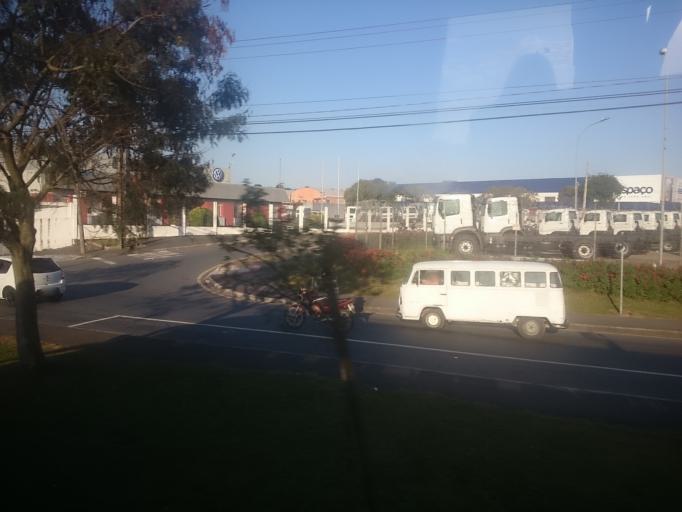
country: BR
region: Parana
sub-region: Curitiba
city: Curitiba
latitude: -25.4832
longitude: -49.2650
